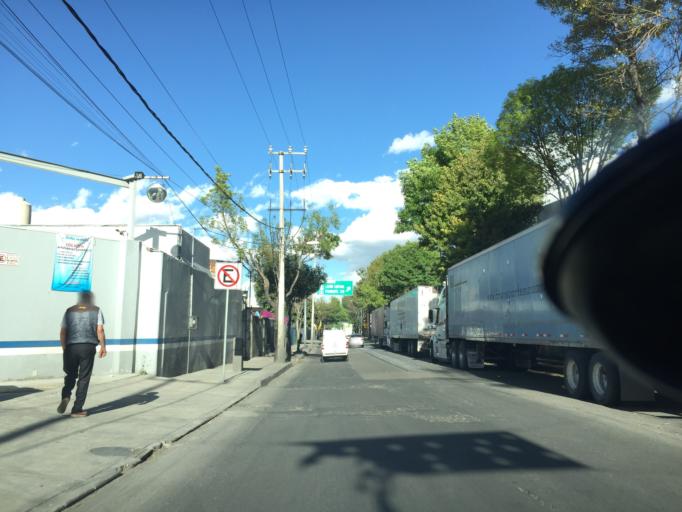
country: MX
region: Mexico City
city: Azcapotzalco
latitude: 19.4882
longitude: -99.1586
